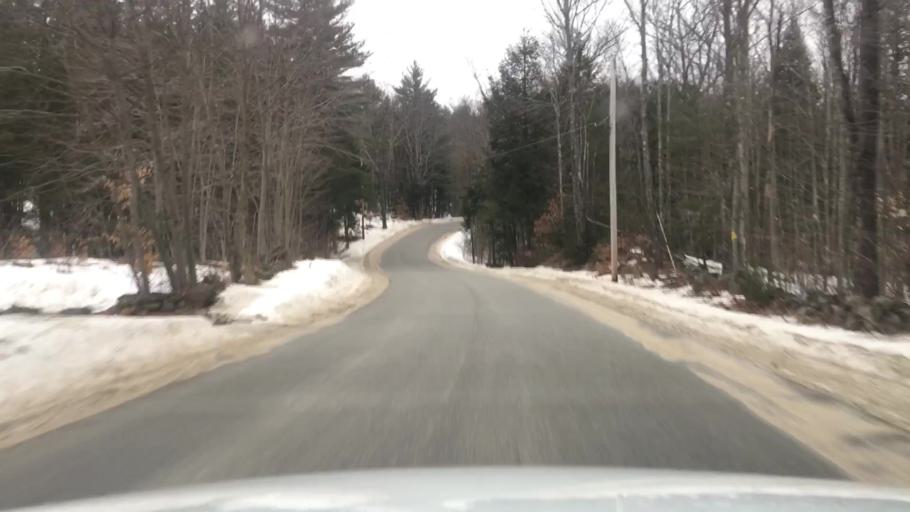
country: US
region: Maine
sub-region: York County
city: Springvale
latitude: 43.5005
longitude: -70.8197
